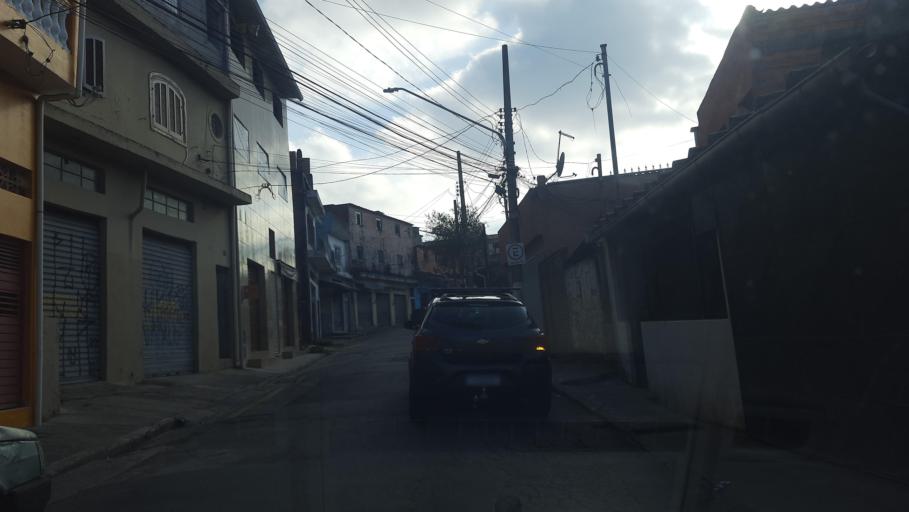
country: BR
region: Sao Paulo
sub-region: Caieiras
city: Caieiras
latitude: -23.4569
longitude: -46.7184
